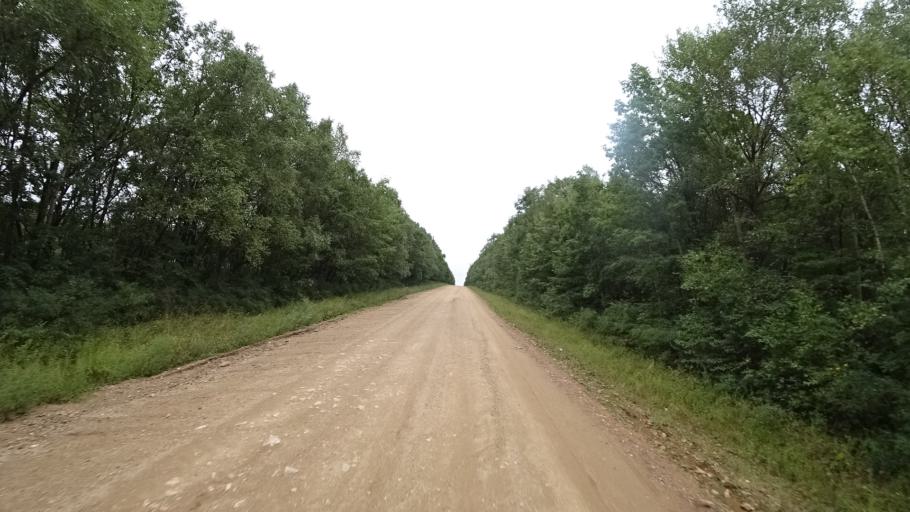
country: RU
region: Primorskiy
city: Ivanovka
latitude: 44.0293
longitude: 132.5284
